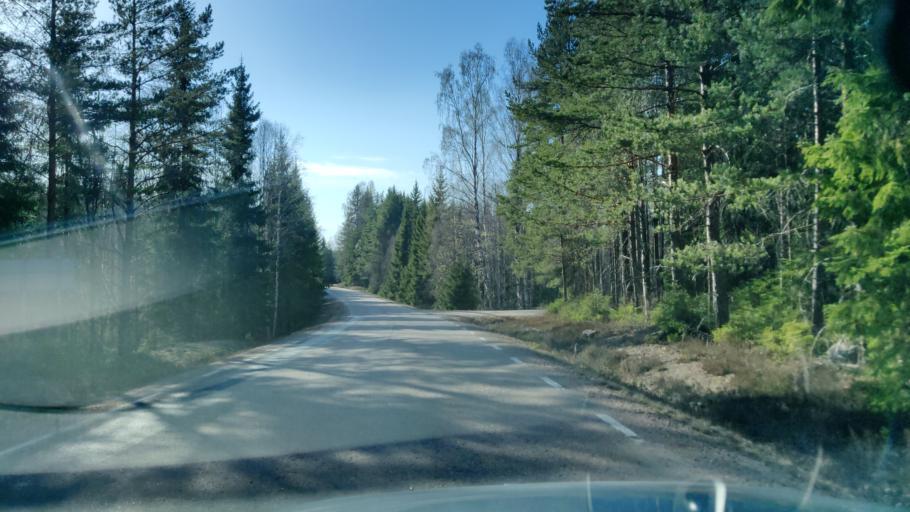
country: SE
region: Vaermland
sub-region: Sunne Kommun
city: Sunne
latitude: 59.9868
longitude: 13.3353
